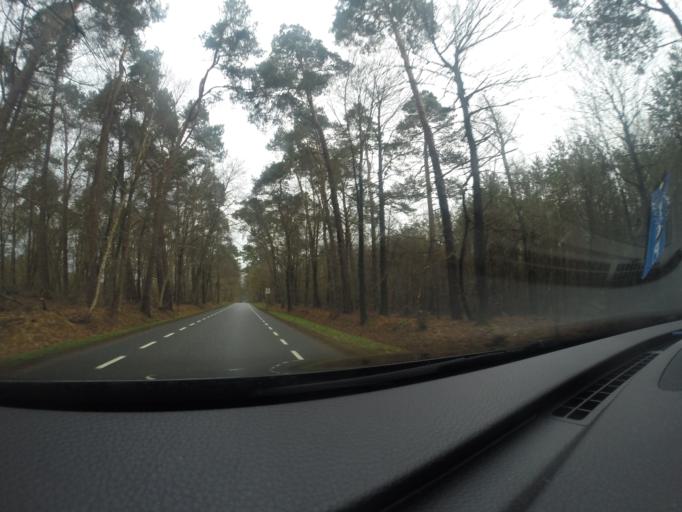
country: NL
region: Overijssel
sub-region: Gemeente Hof van Twente
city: Delden
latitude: 52.2447
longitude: 6.7246
